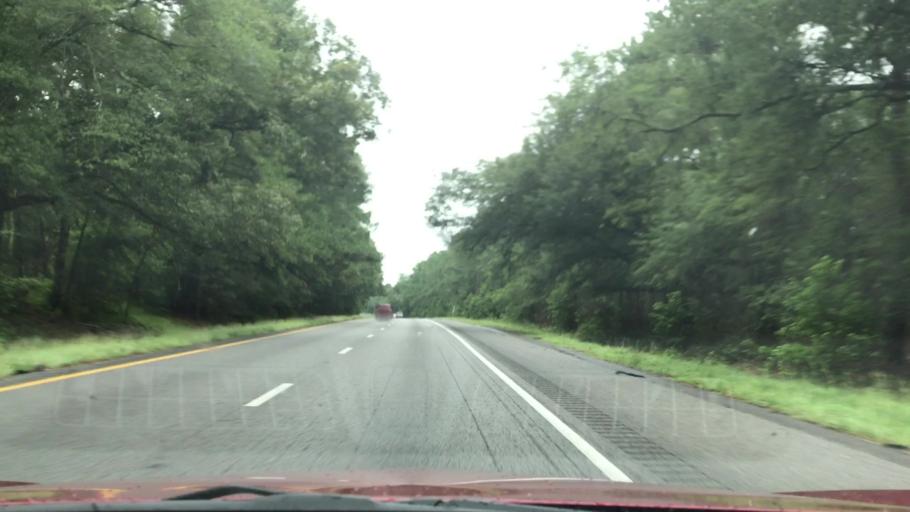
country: US
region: South Carolina
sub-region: Dorchester County
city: Ridgeville
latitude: 33.1549
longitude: -80.3470
